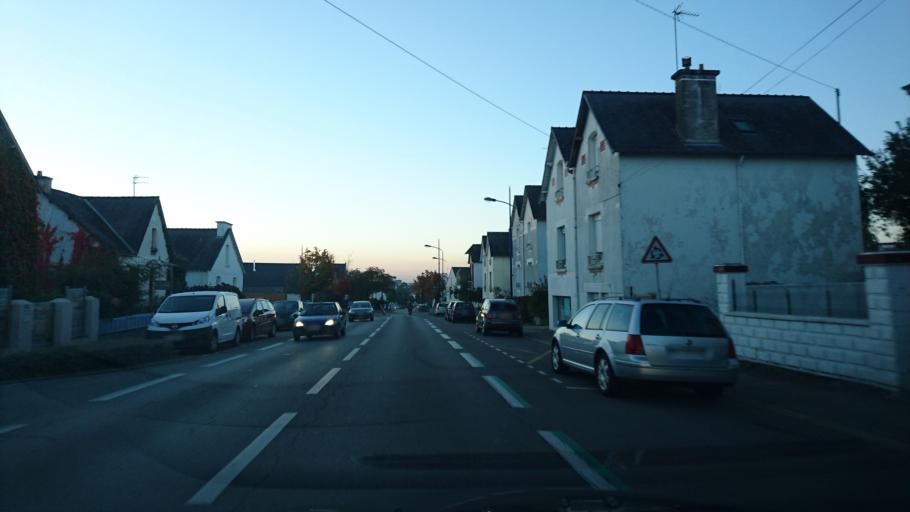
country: FR
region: Brittany
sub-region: Departement du Morbihan
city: Auray
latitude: 47.6722
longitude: -2.9963
